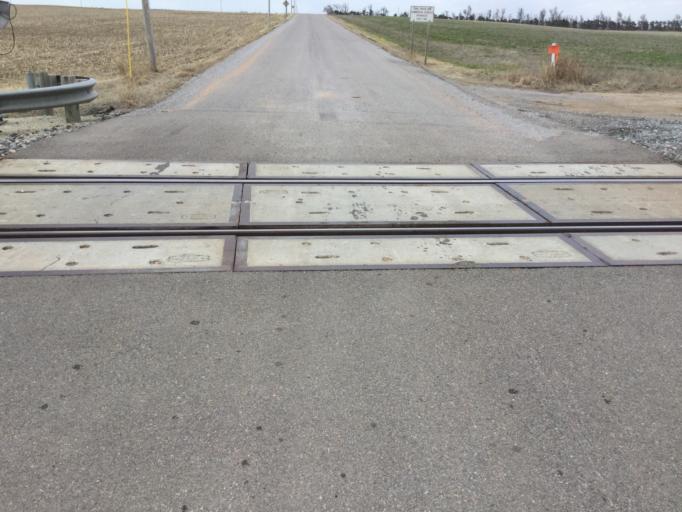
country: US
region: Kansas
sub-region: Kiowa County
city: Greensburg
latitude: 37.6107
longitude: -99.1771
